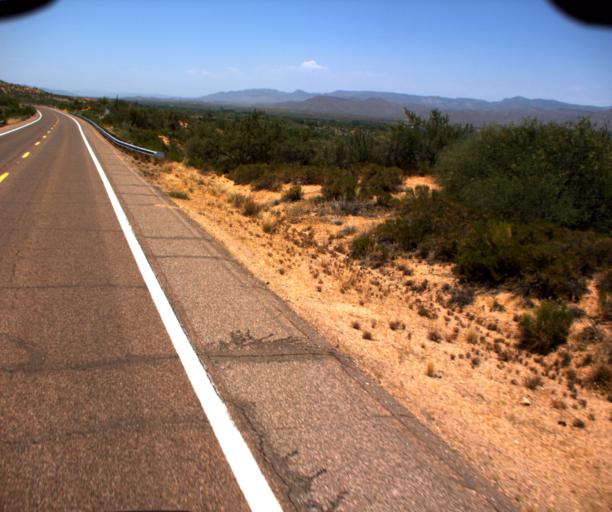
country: US
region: Arizona
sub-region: Gila County
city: Tonto Basin
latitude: 33.7708
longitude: -111.2598
